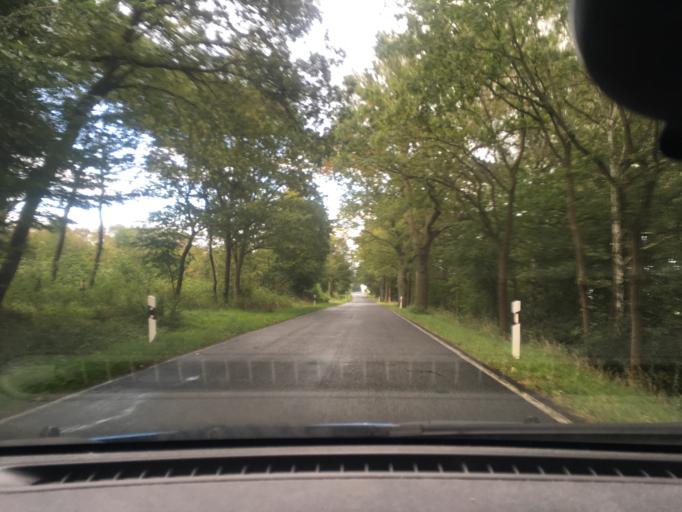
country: DE
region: Lower Saxony
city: Neu Darchau
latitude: 53.3315
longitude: 10.8757
